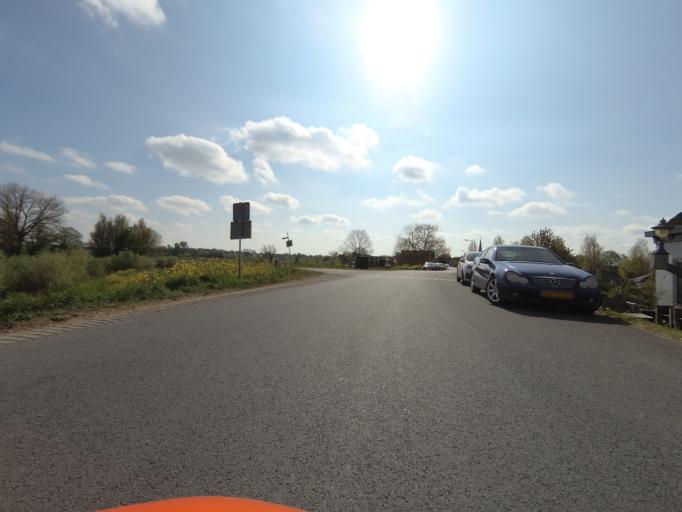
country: NL
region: Utrecht
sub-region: Gemeente IJsselstein
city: IJsselstein
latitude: 51.9659
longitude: 5.0327
